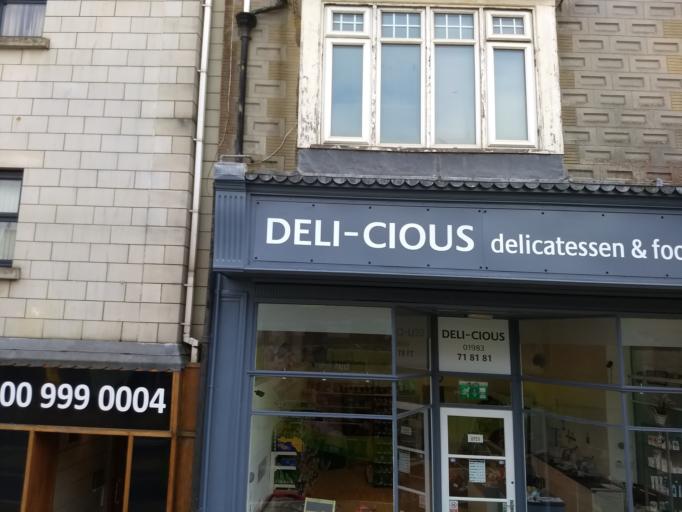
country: GB
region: England
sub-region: Isle of Wight
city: Shanklin
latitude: 50.6295
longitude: -1.1782
